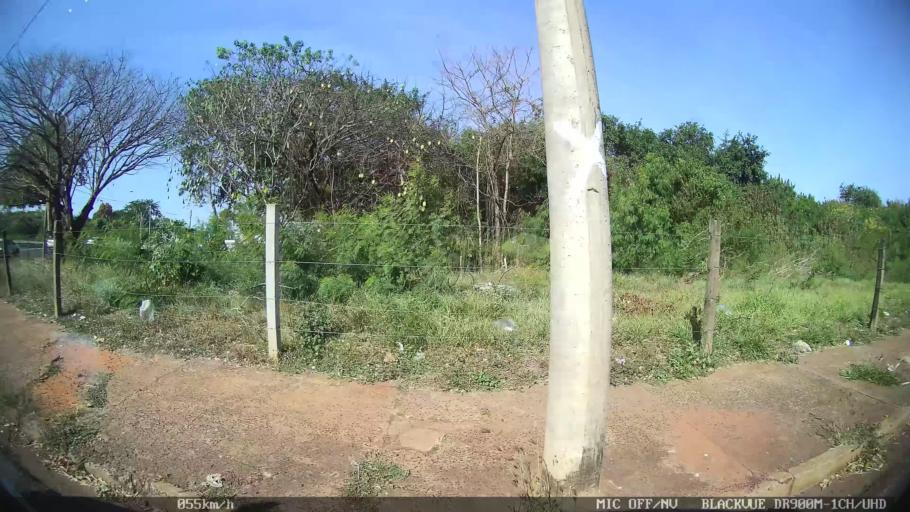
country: BR
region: Sao Paulo
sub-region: Sao Jose Do Rio Preto
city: Sao Jose do Rio Preto
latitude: -20.7838
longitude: -49.3831
